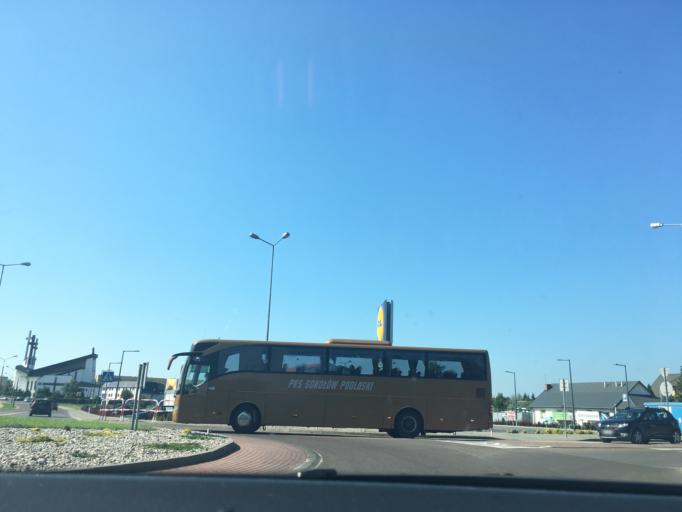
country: PL
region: Lublin Voivodeship
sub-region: Powiat radzynski
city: Radzyn Podlaski
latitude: 51.7826
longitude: 22.6066
